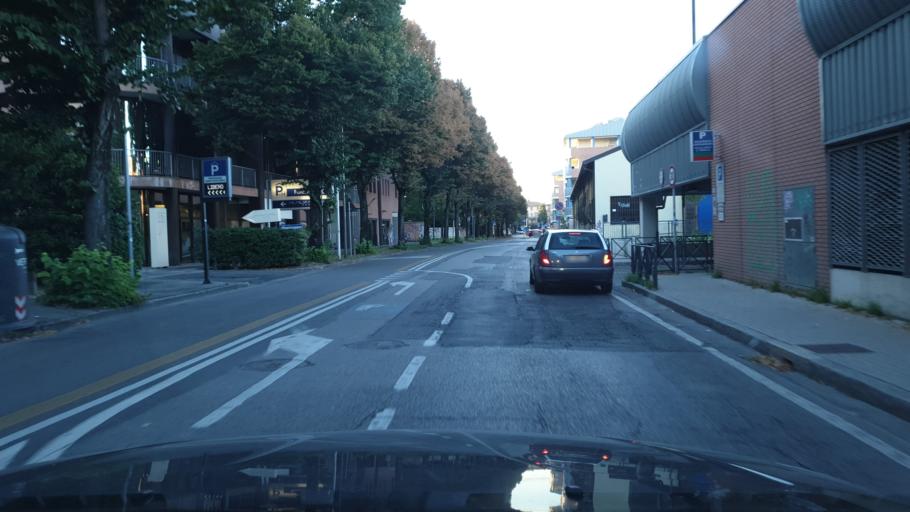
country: IT
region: Emilia-Romagna
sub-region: Provincia di Bologna
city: Bologna
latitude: 44.4946
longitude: 11.3603
